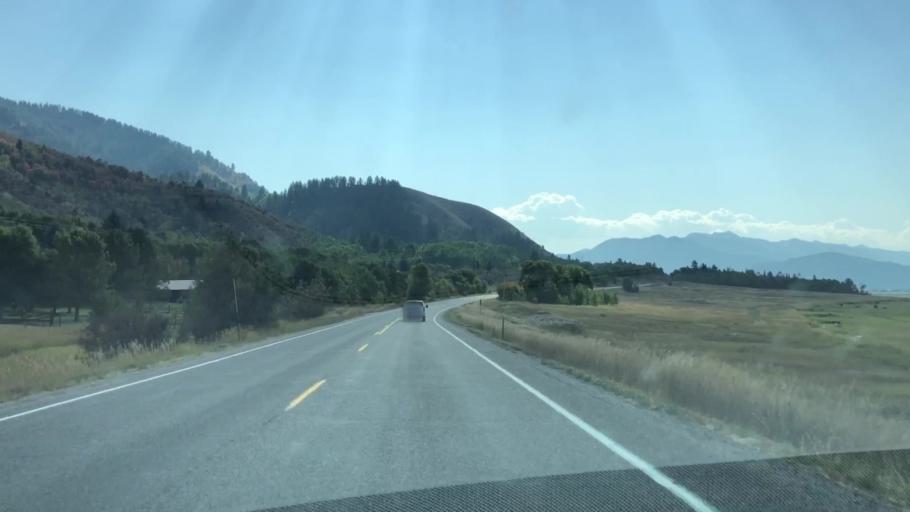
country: US
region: Wyoming
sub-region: Teton County
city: Hoback
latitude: 43.2168
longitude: -111.0659
